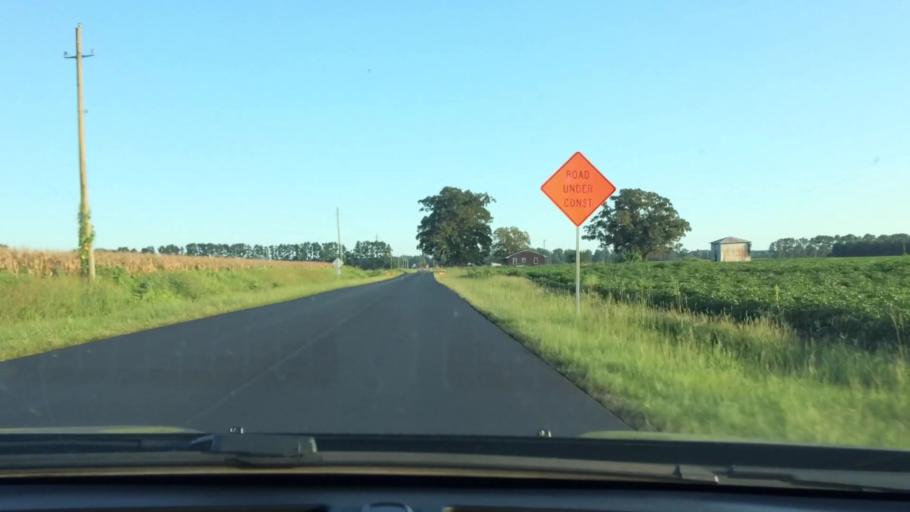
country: US
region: North Carolina
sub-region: Pitt County
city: Ayden
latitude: 35.4416
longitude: -77.4535
